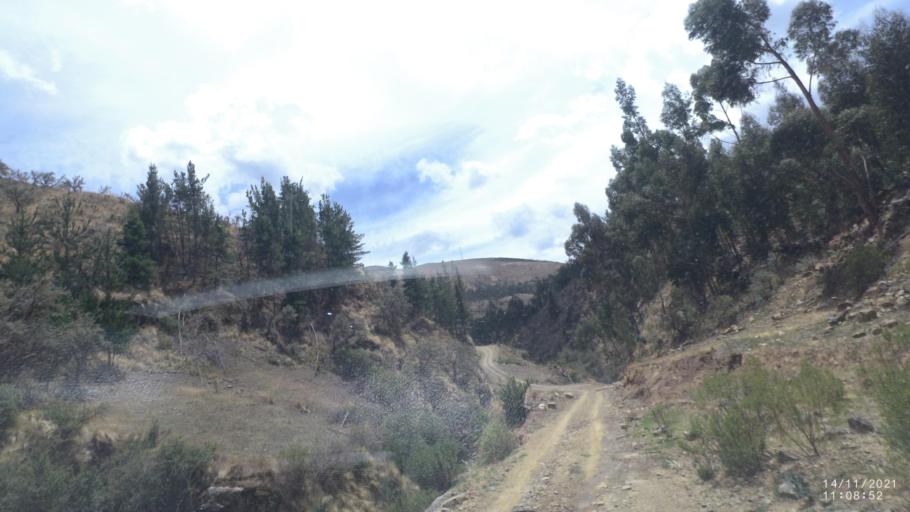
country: BO
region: Cochabamba
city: Cochabamba
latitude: -17.3316
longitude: -66.0550
